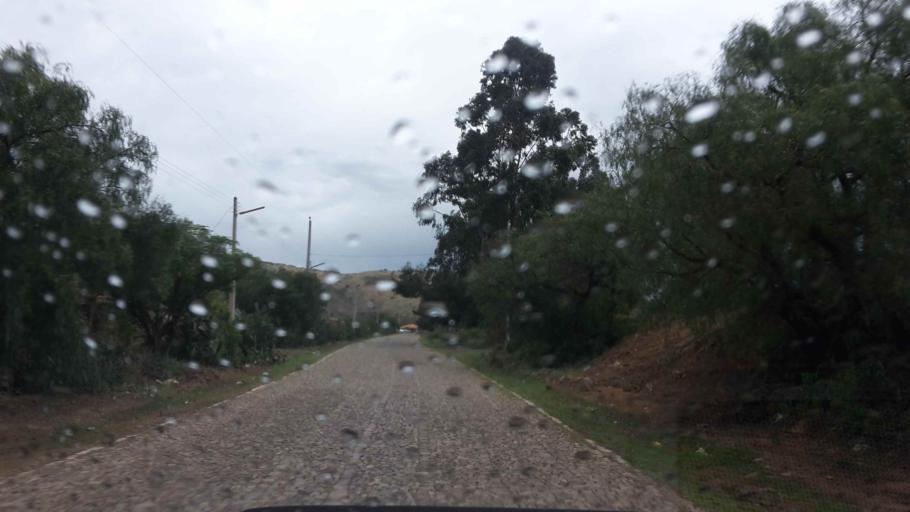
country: BO
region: Cochabamba
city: Cochabamba
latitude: -17.5496
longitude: -66.1721
